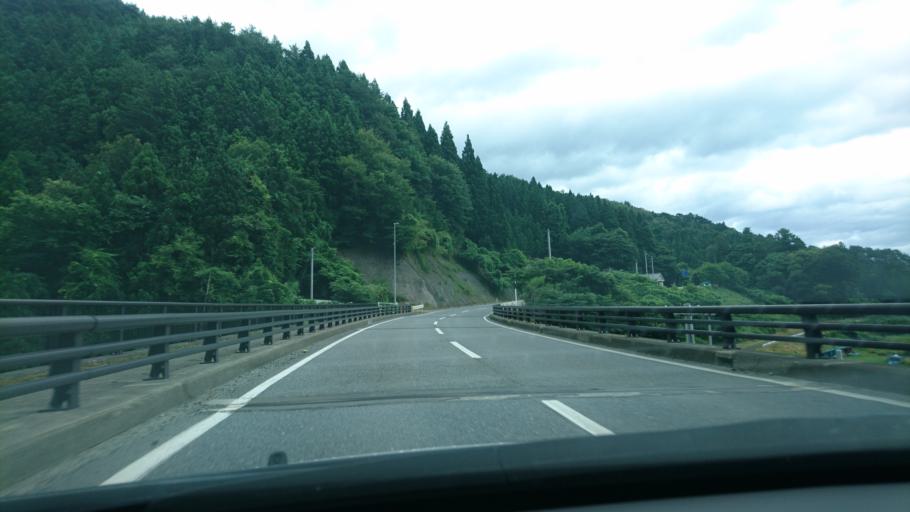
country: JP
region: Iwate
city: Kamaishi
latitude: 39.1921
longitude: 141.8580
